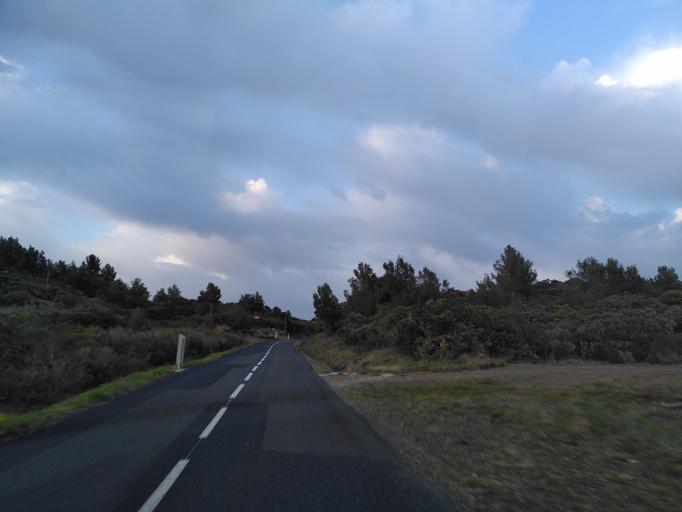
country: FR
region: Languedoc-Roussillon
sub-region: Departement des Pyrenees-Orientales
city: Estagel
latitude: 42.8208
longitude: 2.7098
